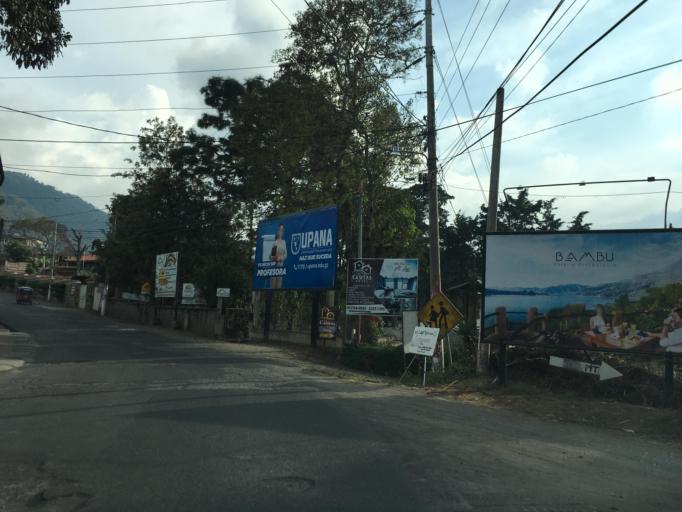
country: GT
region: Solola
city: Santiago Atitlan
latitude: 14.6482
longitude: -91.2284
